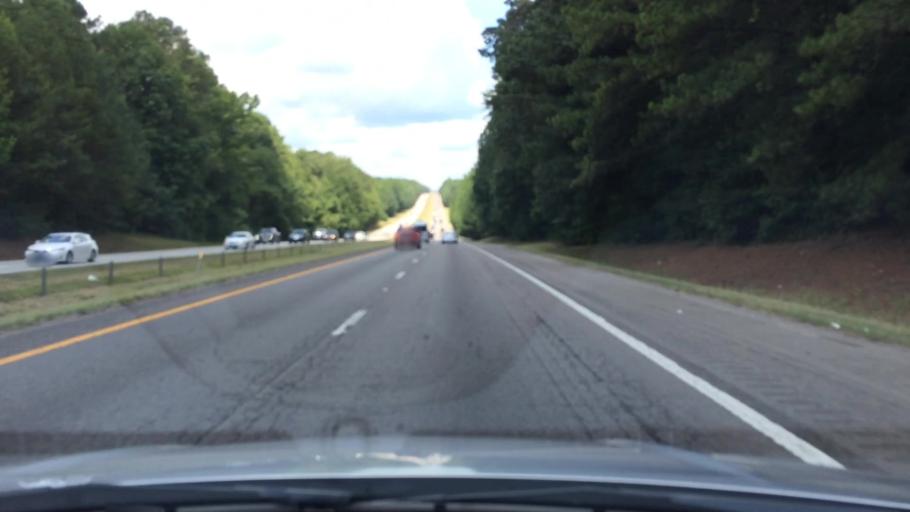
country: US
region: South Carolina
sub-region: Lexington County
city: Chapin
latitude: 34.1848
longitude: -81.3350
